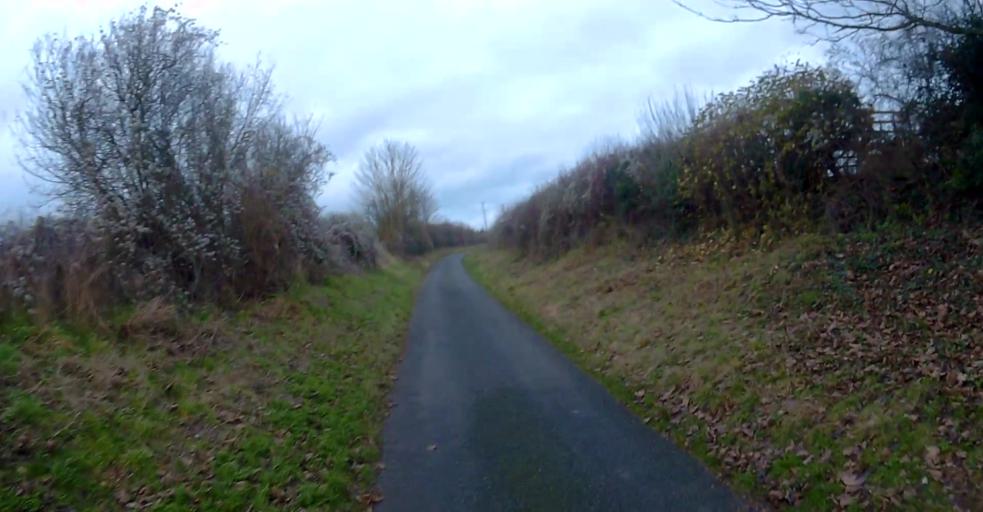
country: GB
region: England
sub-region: Hampshire
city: Overton
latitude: 51.2531
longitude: -1.2550
